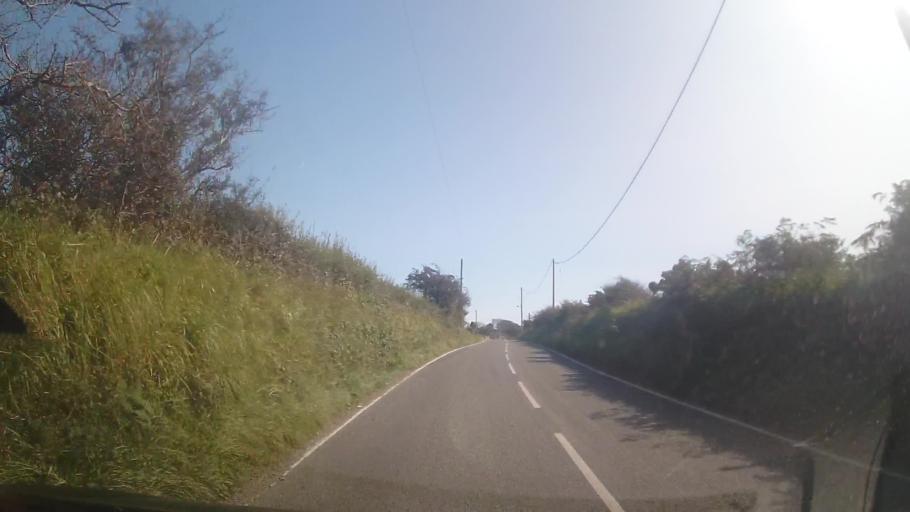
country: GB
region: Wales
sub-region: Pembrokeshire
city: Scleddau
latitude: 51.9315
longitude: -5.0086
